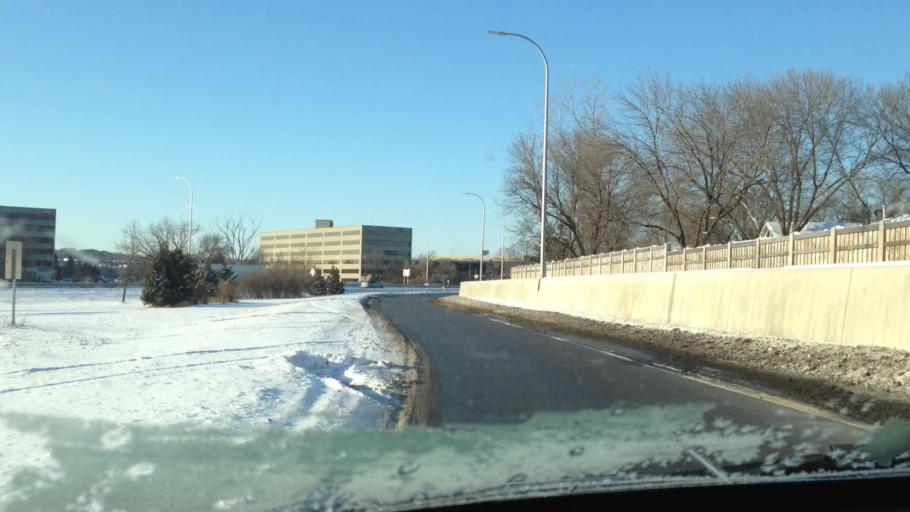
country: US
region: Minnesota
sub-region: Hennepin County
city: Edina
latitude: 44.8651
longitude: -93.3484
